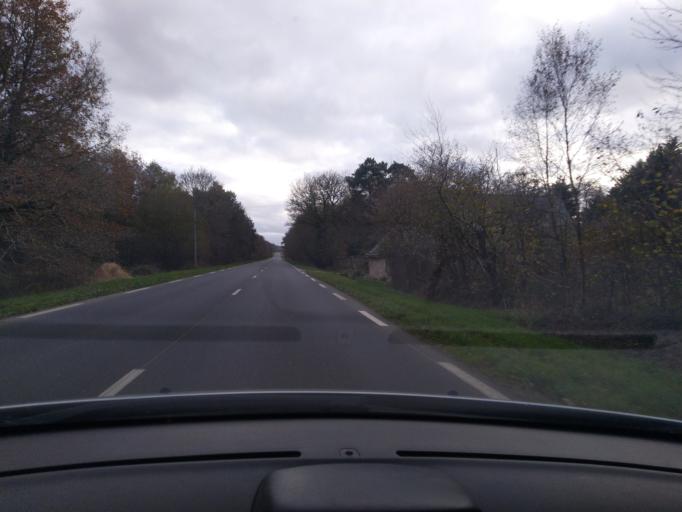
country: FR
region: Brittany
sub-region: Departement des Cotes-d'Armor
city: Plounevez-Moedec
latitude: 48.5771
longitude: -3.4949
